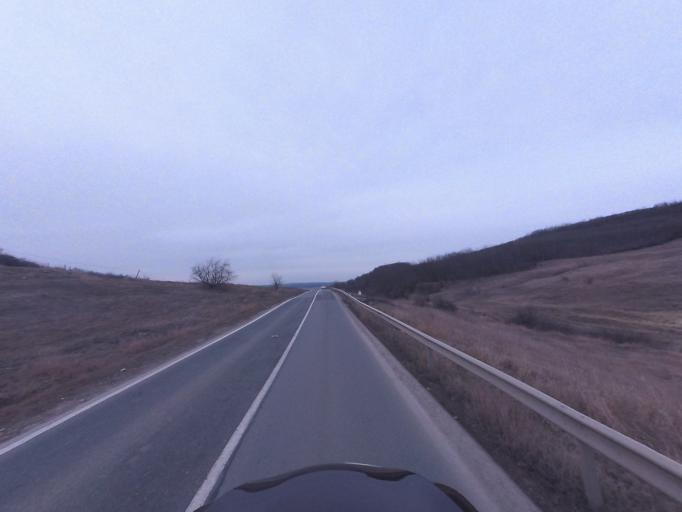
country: RO
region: Iasi
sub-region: Comuna Popricani
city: Popricani
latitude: 47.2971
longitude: 27.5101
